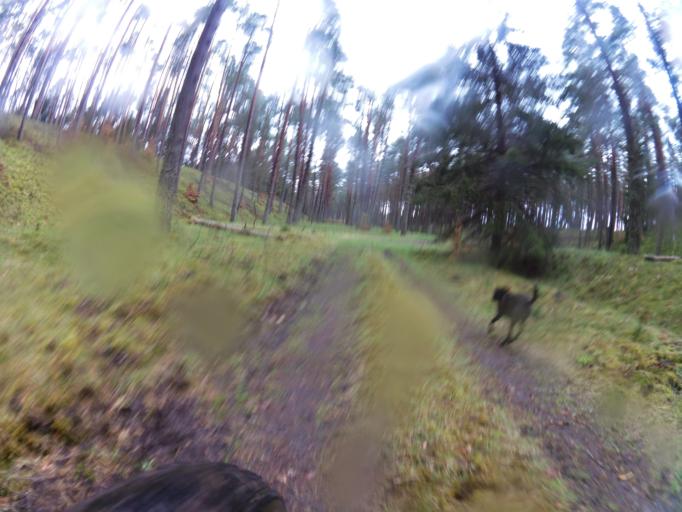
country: PL
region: Pomeranian Voivodeship
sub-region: Powiat slupski
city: Kepice
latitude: 54.2520
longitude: 16.7905
